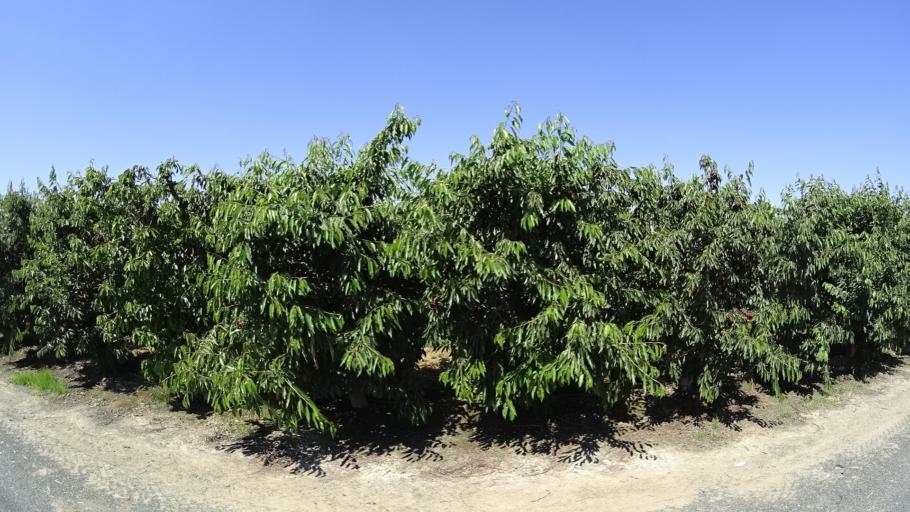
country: US
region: California
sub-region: Fresno County
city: Laton
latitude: 36.4365
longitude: -119.6186
